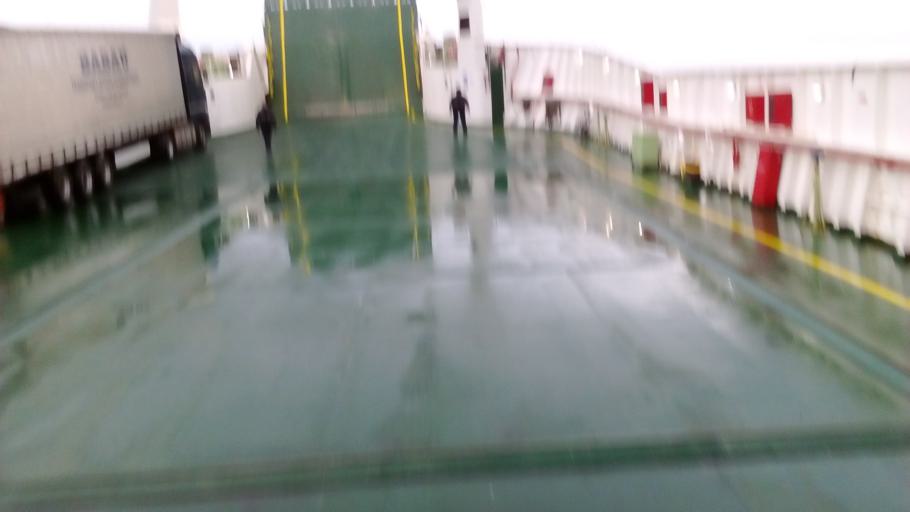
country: IT
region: Sicily
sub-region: Messina
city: Larderia
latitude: 38.1322
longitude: 15.5241
